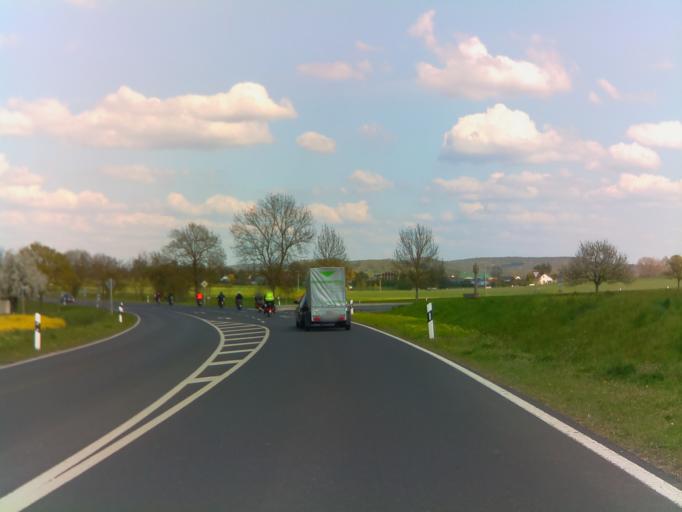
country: DE
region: Bavaria
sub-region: Regierungsbezirk Unterfranken
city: Bad Konigshofen im Grabfeld
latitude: 50.2927
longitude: 10.4534
